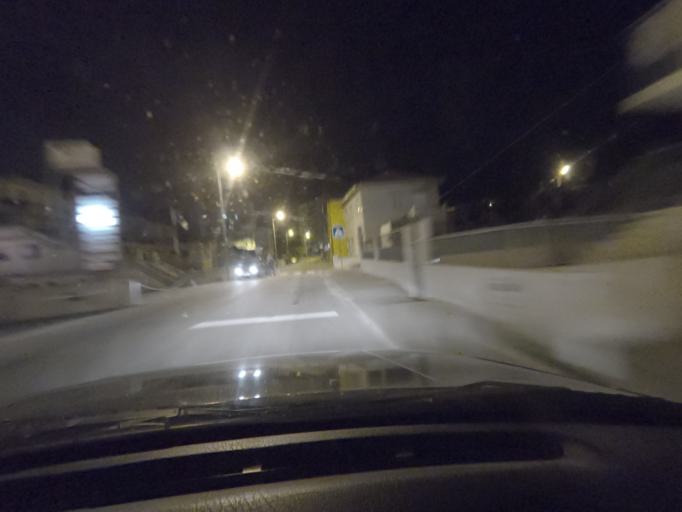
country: PT
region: Vila Real
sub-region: Peso da Regua
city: Godim
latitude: 41.1691
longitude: -7.7964
